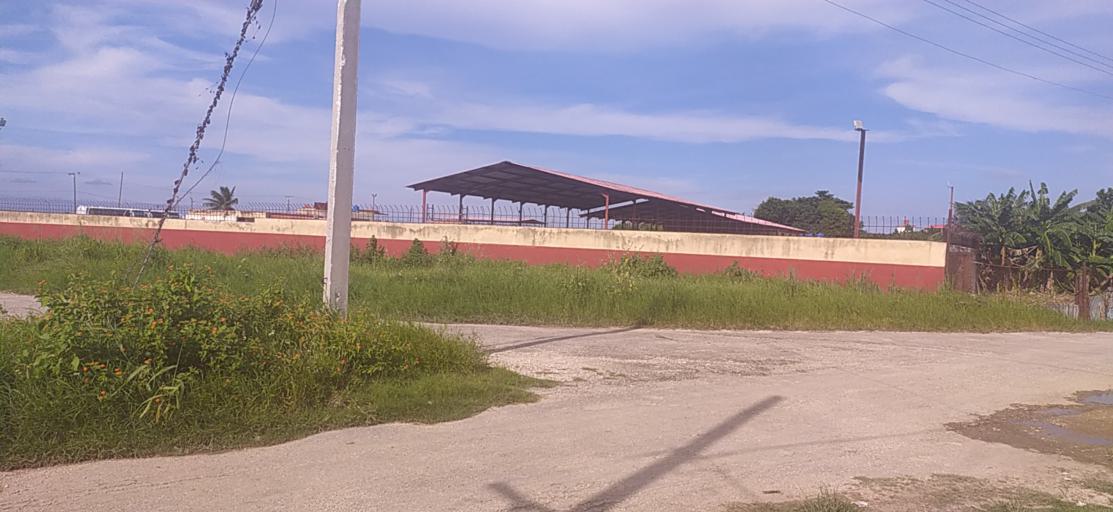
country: CU
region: La Habana
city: Habana del Este
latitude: 23.1673
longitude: -82.3057
